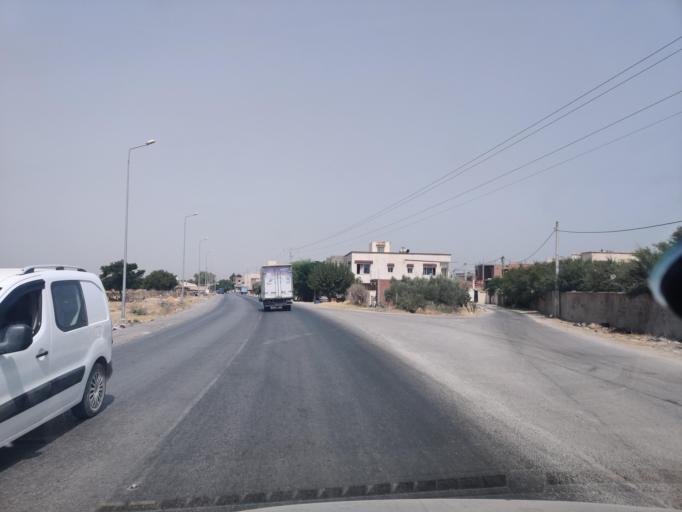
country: TN
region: Tunis
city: La Sebala du Mornag
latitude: 36.6581
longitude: 10.3305
